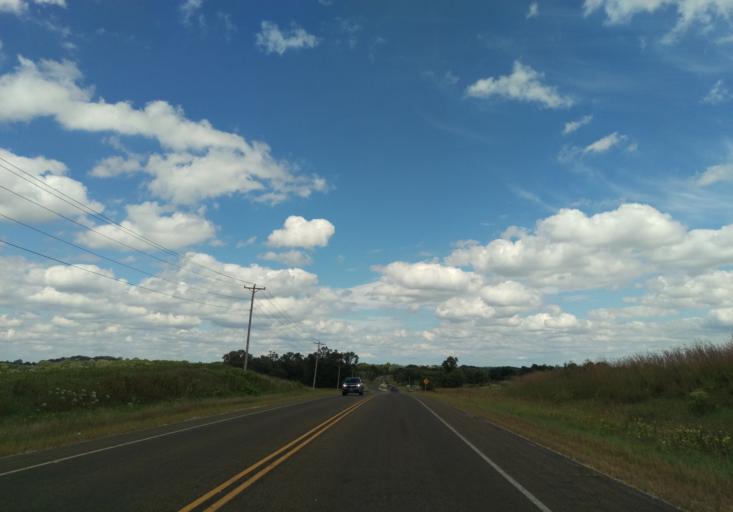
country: US
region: Wisconsin
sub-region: Dane County
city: Shorewood Hills
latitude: 43.1337
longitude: -89.4421
